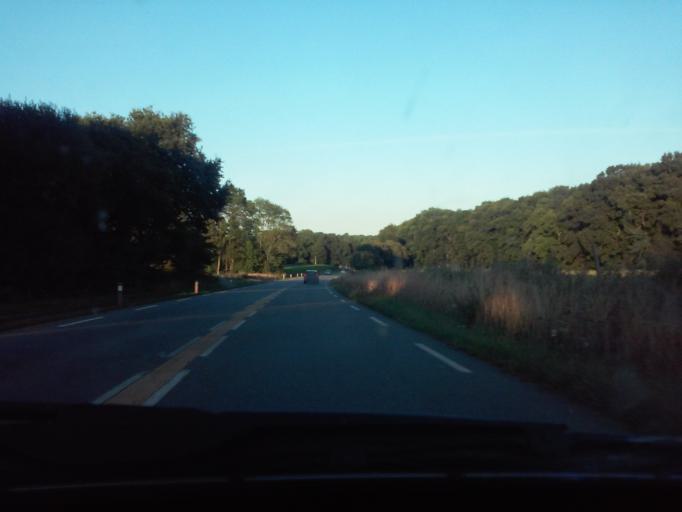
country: FR
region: Brittany
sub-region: Departement des Cotes-d'Armor
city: Lanvallay
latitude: 48.4503
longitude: -2.0055
